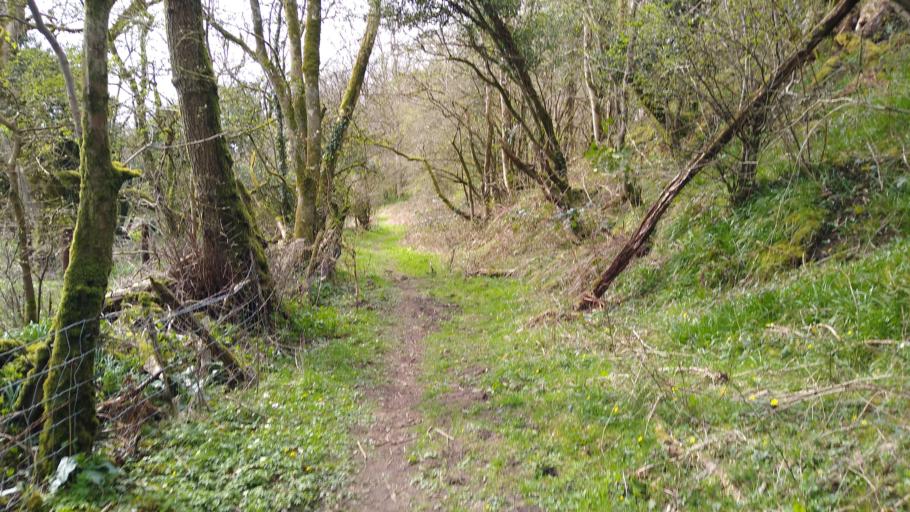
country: GB
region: England
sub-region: Cumbria
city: Dearham
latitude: 54.6748
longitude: -3.4102
